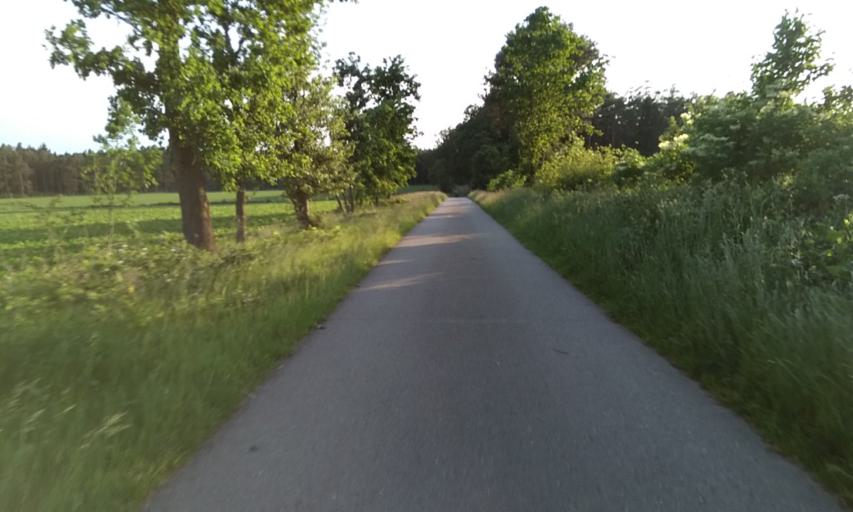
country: DE
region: Lower Saxony
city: Dollern
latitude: 53.5331
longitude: 9.5225
